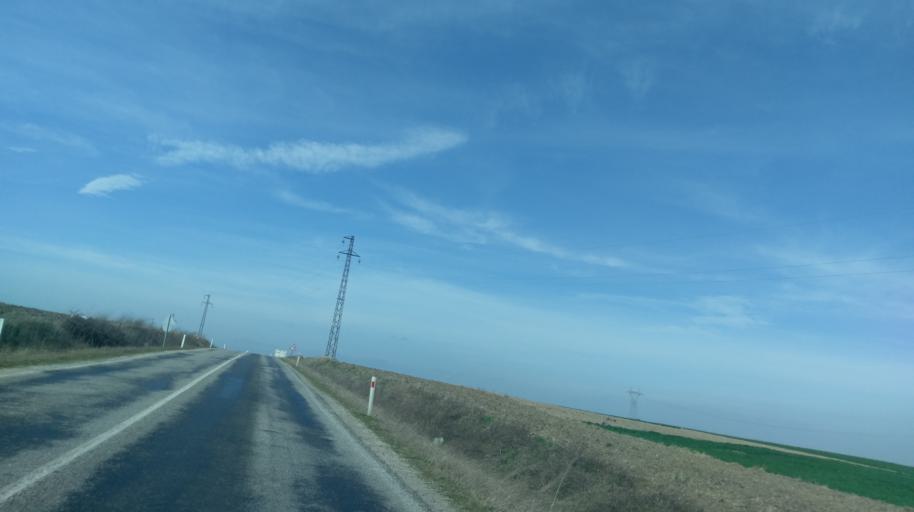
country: TR
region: Edirne
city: Uzun Keupru
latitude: 41.2754
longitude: 26.7419
